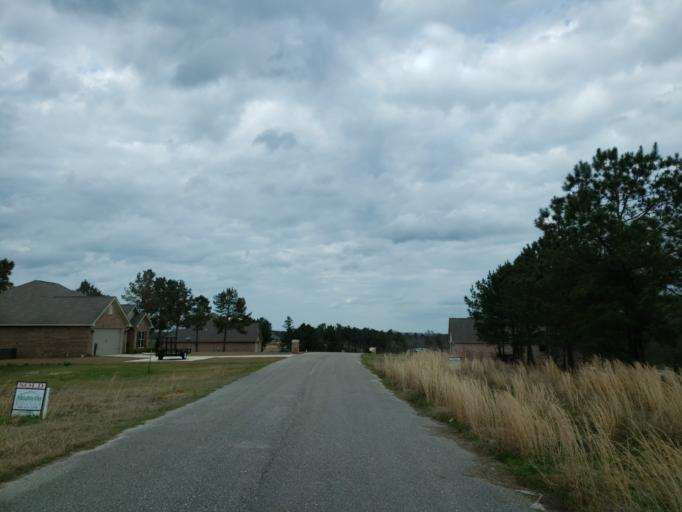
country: US
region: Mississippi
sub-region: Jones County
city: Ellisville
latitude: 31.5547
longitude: -89.2538
